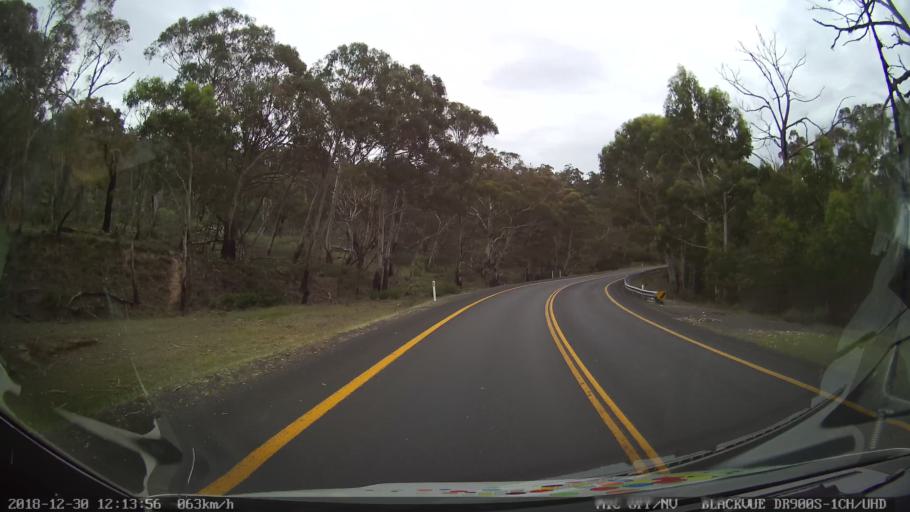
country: AU
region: New South Wales
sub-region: Snowy River
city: Jindabyne
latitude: -36.3472
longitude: 148.5799
